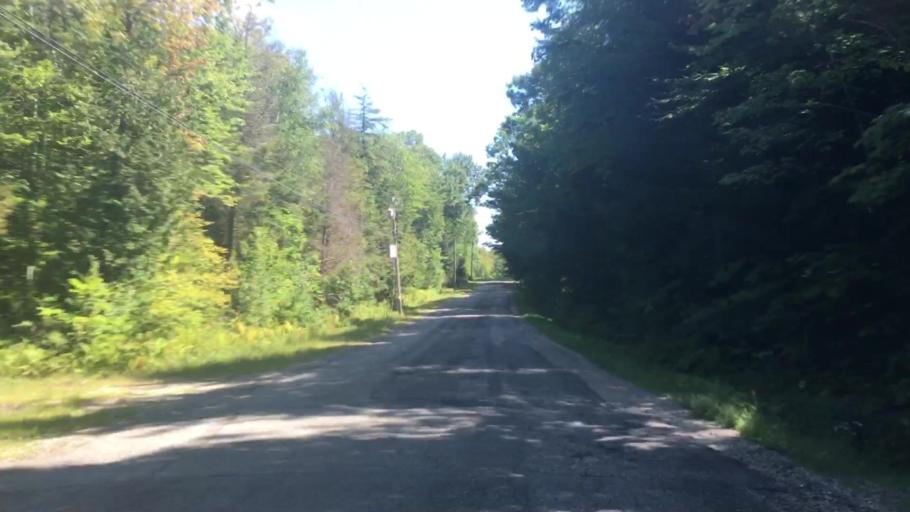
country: US
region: Maine
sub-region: Androscoggin County
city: Sabattus
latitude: 44.1218
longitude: -70.0558
